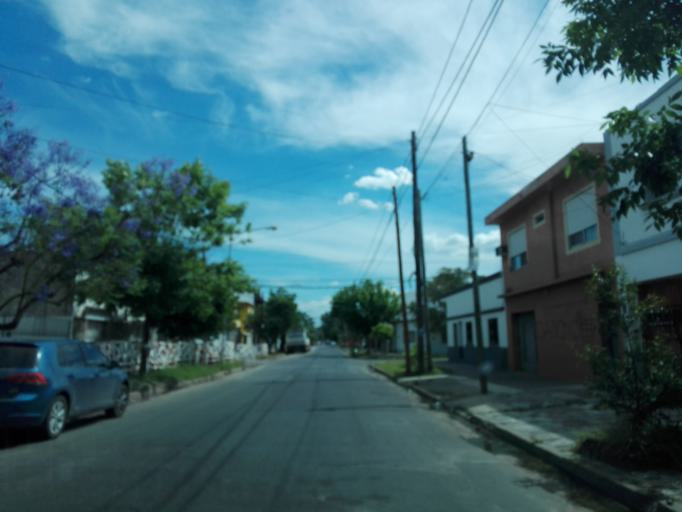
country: AR
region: Buenos Aires
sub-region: Partido de Lanus
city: Lanus
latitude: -34.7198
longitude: -58.3844
